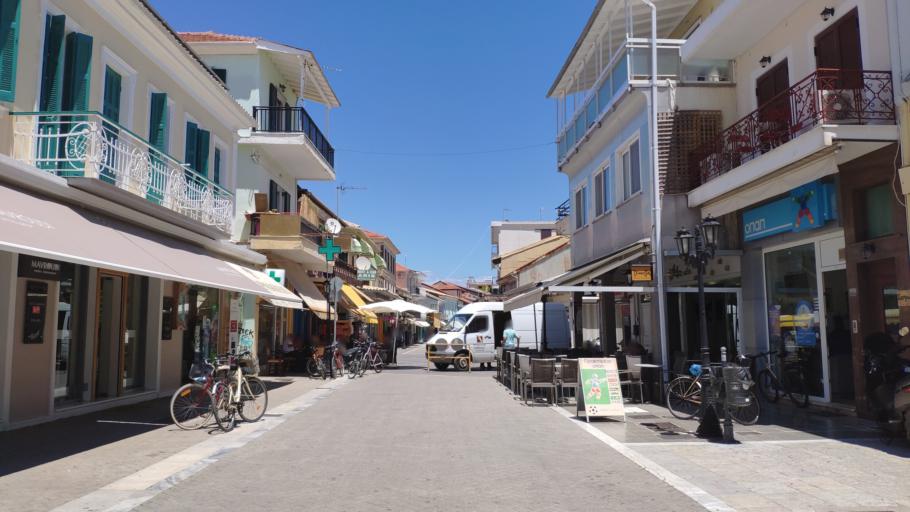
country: GR
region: Ionian Islands
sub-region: Lefkada
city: Lefkada
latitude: 38.8326
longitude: 20.7064
